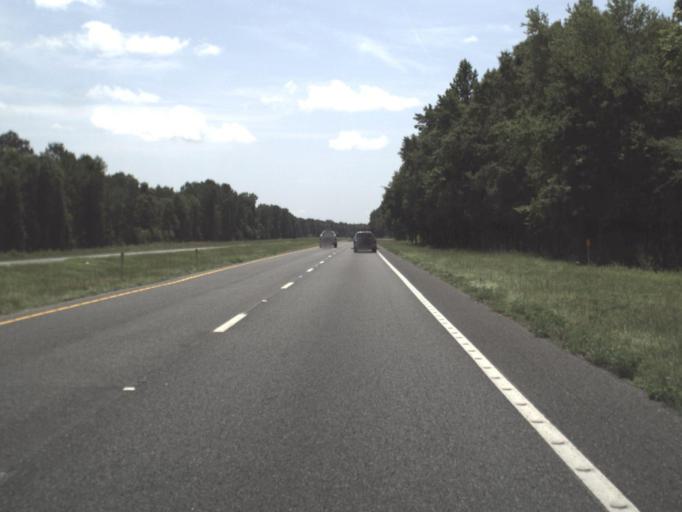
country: US
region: Florida
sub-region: Taylor County
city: Perry
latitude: 30.0005
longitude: -83.5081
